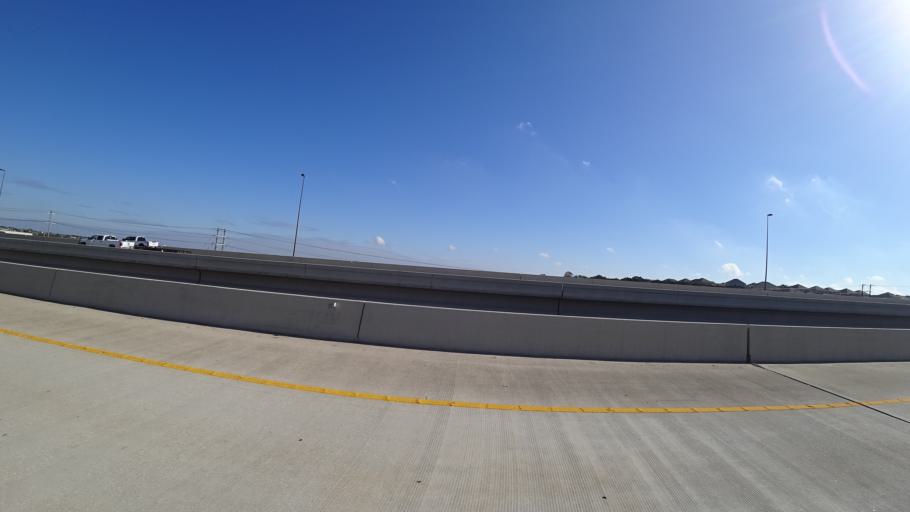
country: US
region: Texas
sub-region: Williamson County
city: Cedar Park
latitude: 30.4969
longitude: -97.8034
